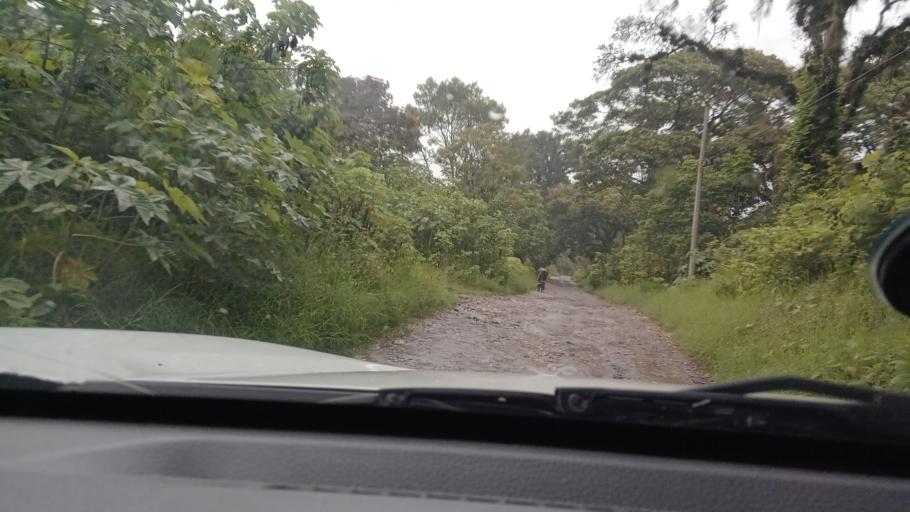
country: MX
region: Veracruz
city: Coatepec
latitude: 19.4557
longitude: -96.9763
